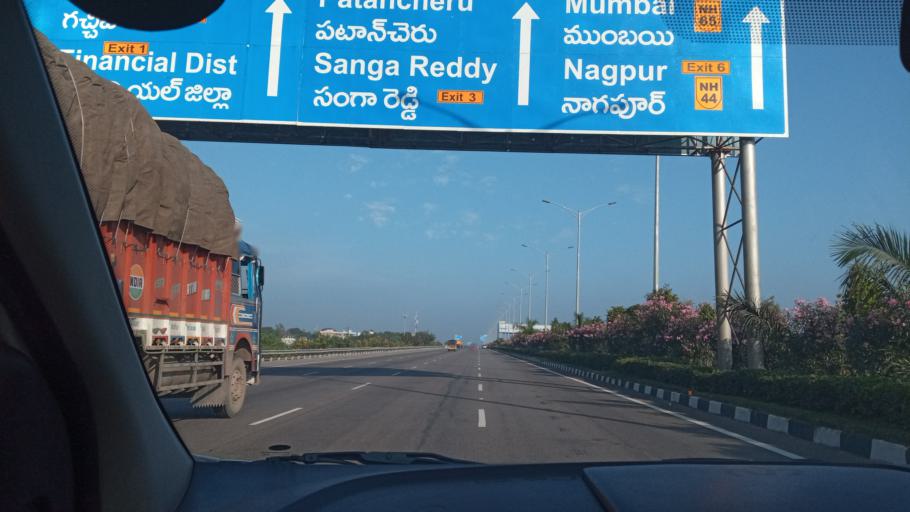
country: IN
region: Telangana
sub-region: Hyderabad
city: Hyderabad
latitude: 17.3368
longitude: 78.3675
